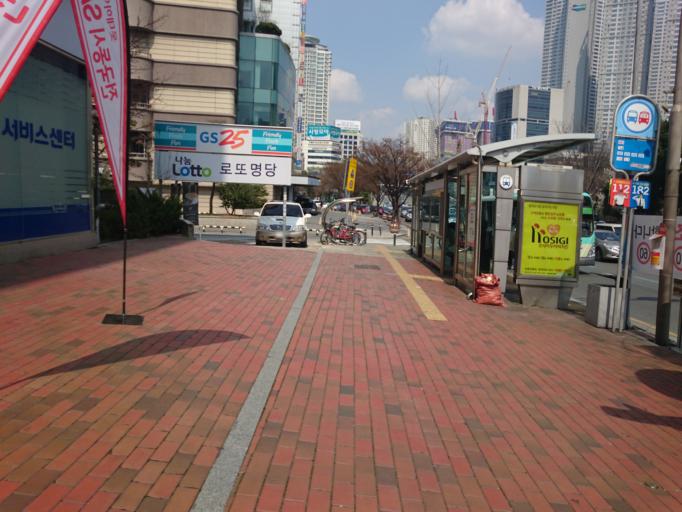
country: KR
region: Daegu
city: Daegu
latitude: 35.8571
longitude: 128.6255
